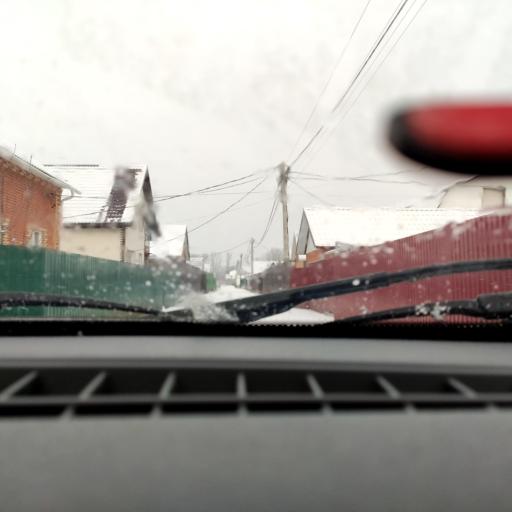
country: RU
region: Bashkortostan
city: Ufa
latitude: 54.6269
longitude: 55.8863
